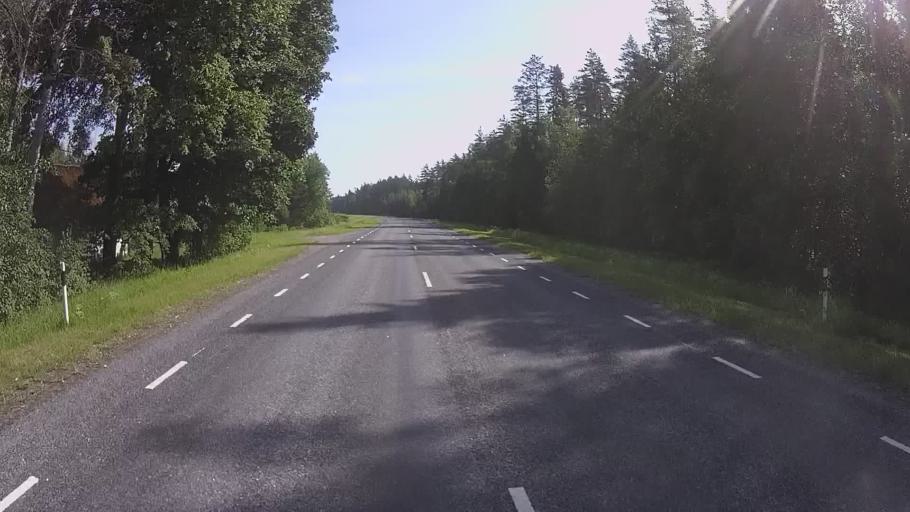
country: EE
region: Valgamaa
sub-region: Torva linn
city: Torva
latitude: 58.0259
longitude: 25.9602
